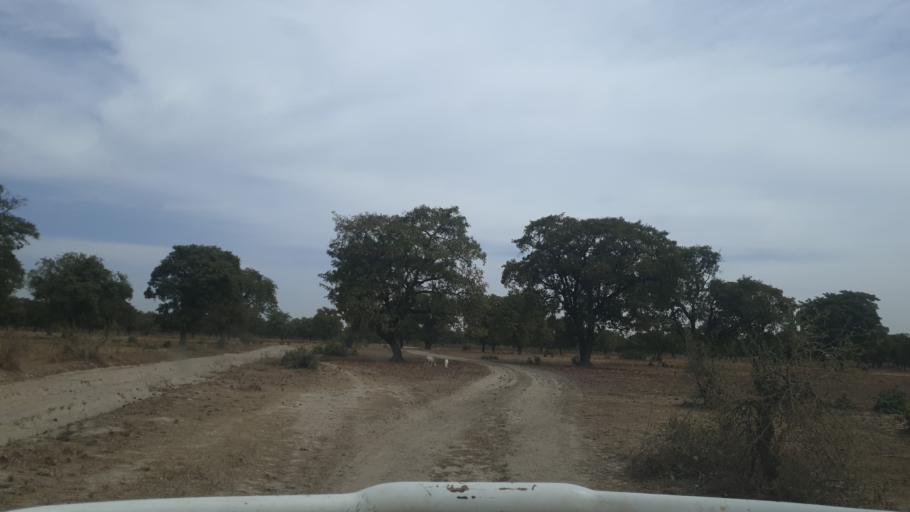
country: ML
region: Sikasso
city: Yorosso
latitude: 12.2388
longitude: -4.7366
